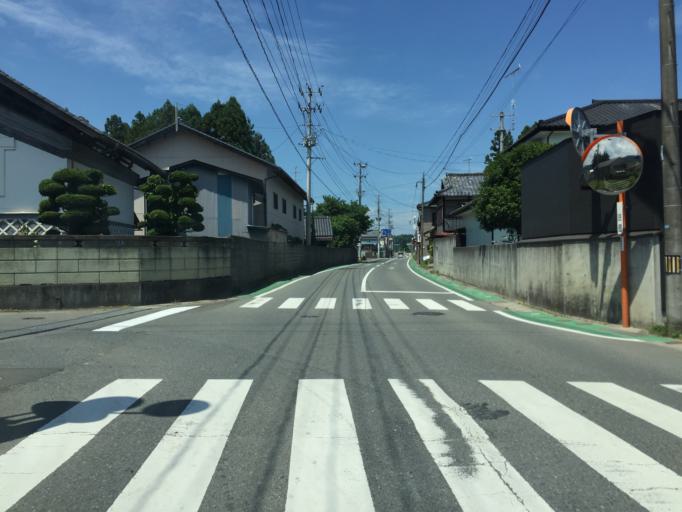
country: JP
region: Fukushima
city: Namie
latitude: 37.7208
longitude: 140.9295
